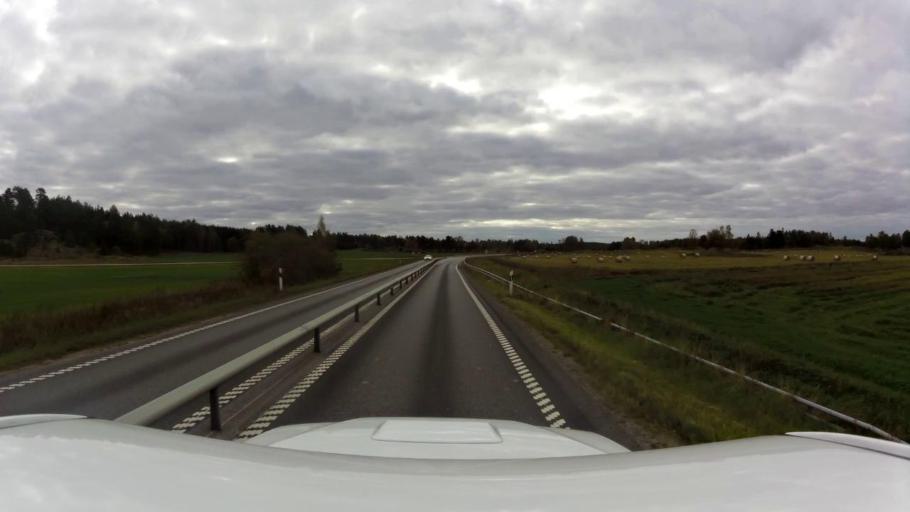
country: SE
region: OEstergoetland
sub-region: Linkopings Kommun
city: Malmslatt
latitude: 58.3239
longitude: 15.5664
